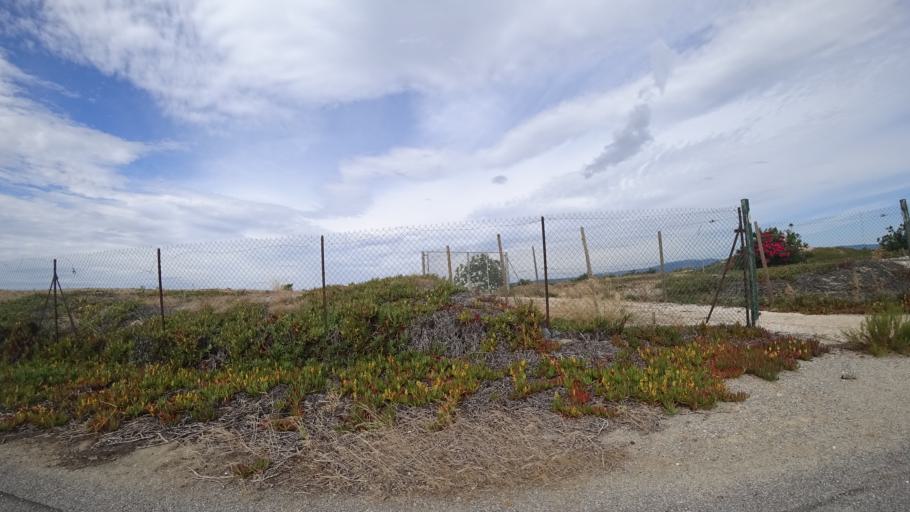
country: FR
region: Languedoc-Roussillon
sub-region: Departement de l'Aude
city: Leucate
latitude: 42.8760
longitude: 3.0416
